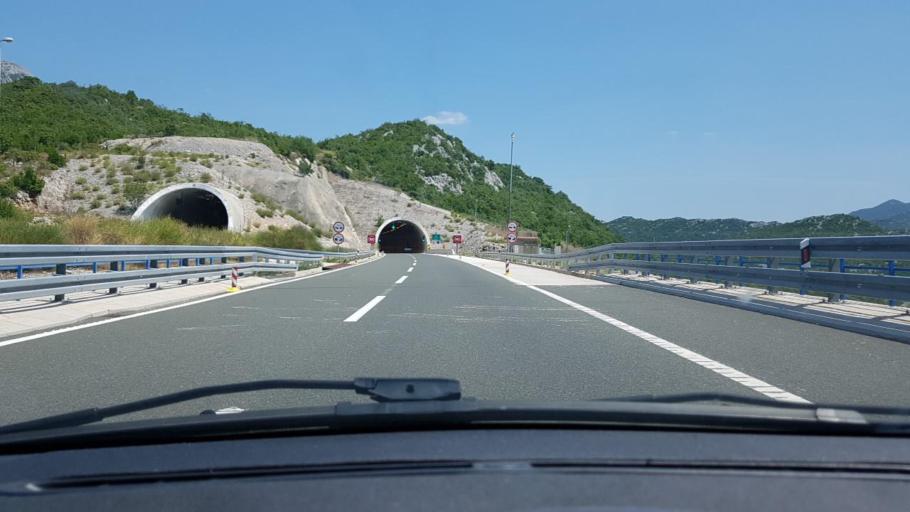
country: HR
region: Splitsko-Dalmatinska
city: Vrgorac
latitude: 43.2055
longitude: 17.2883
